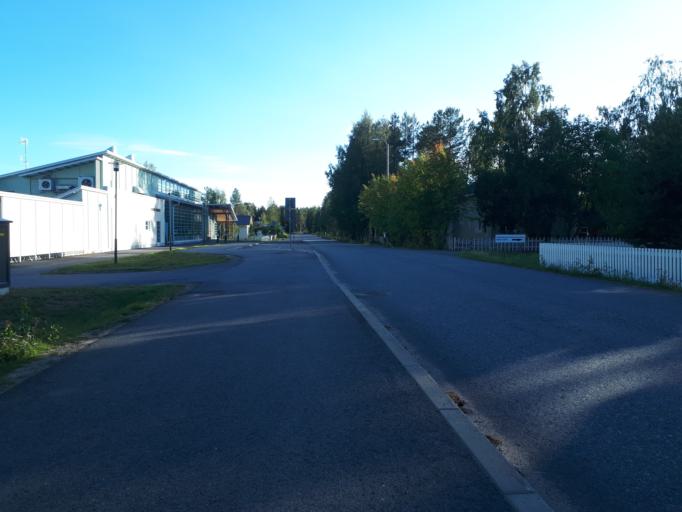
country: FI
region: Northern Ostrobothnia
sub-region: Oulunkaari
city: Ii
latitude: 65.3151
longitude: 25.3864
